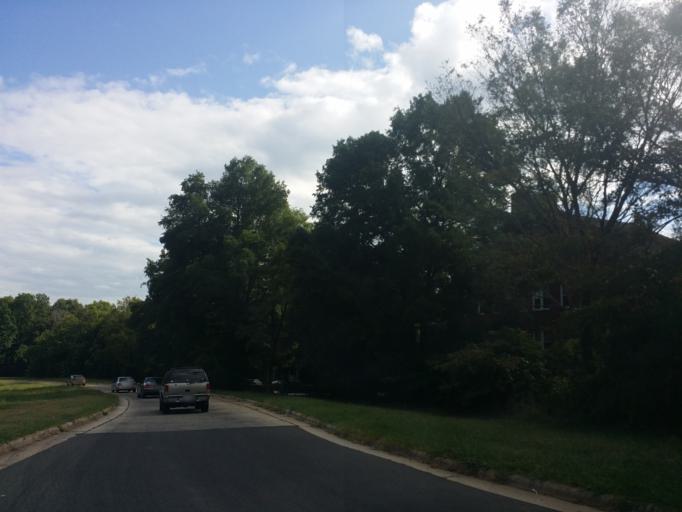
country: US
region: North Carolina
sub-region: Durham County
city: Durham
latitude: 35.9968
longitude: -78.9130
